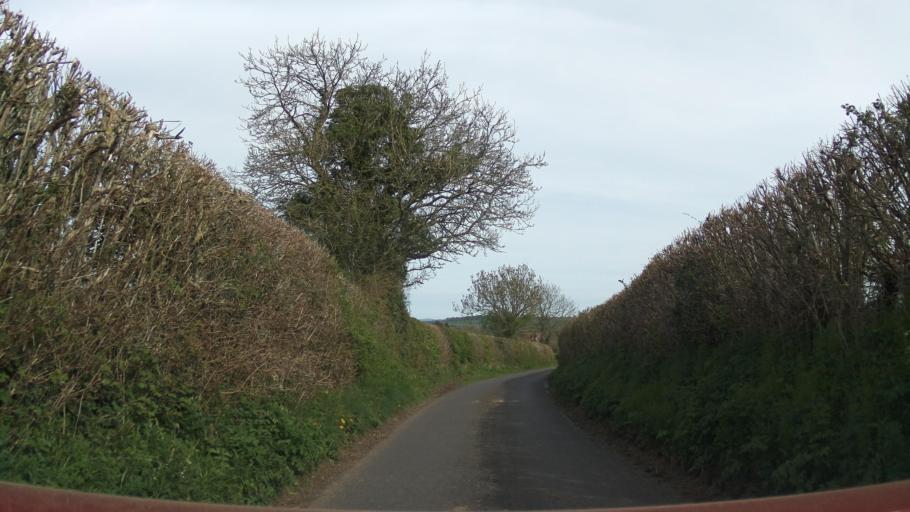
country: GB
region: England
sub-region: Somerset
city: Milborne Port
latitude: 50.9994
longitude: -2.4862
